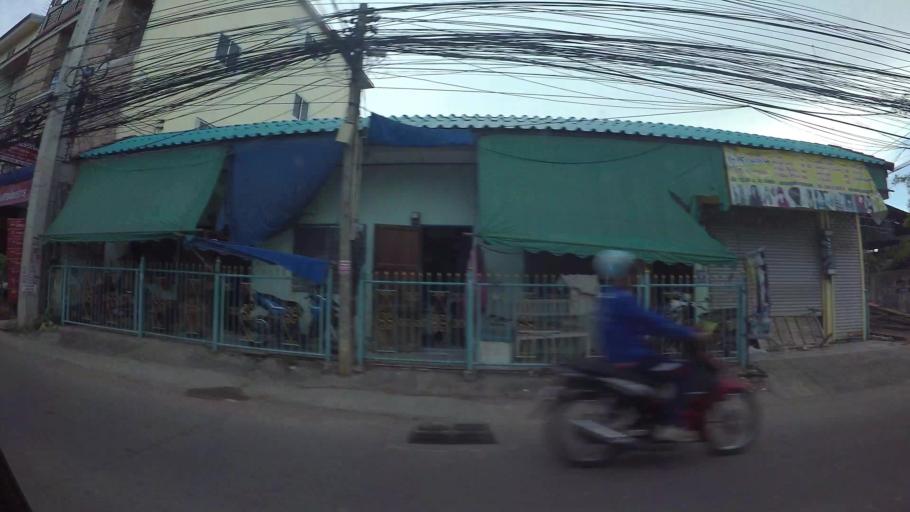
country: TH
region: Chon Buri
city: Phatthaya
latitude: 12.9117
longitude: 100.8857
